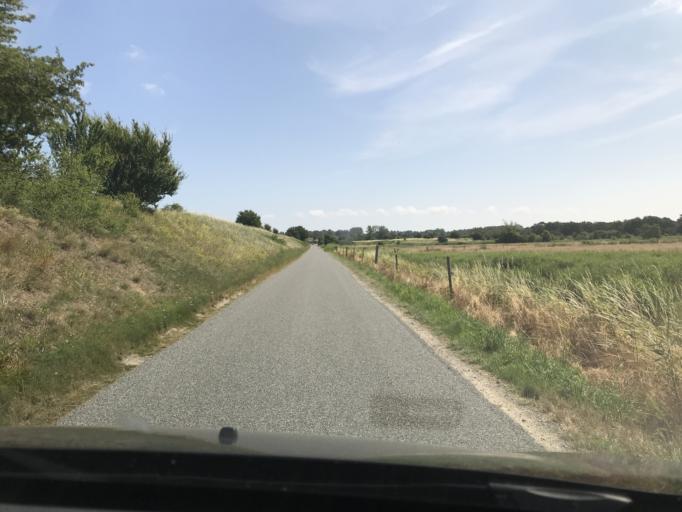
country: DK
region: South Denmark
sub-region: AEro Kommune
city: AEroskobing
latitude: 54.8843
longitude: 10.3747
